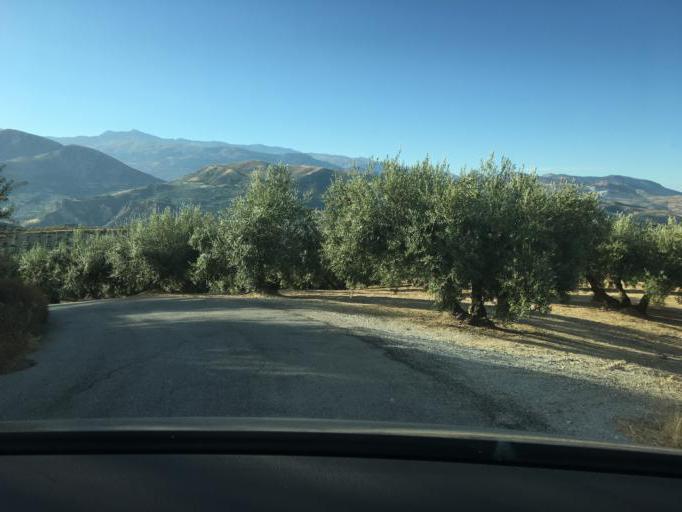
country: ES
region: Andalusia
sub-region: Provincia de Granada
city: Beas de Granada
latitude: 37.2128
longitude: -3.4699
